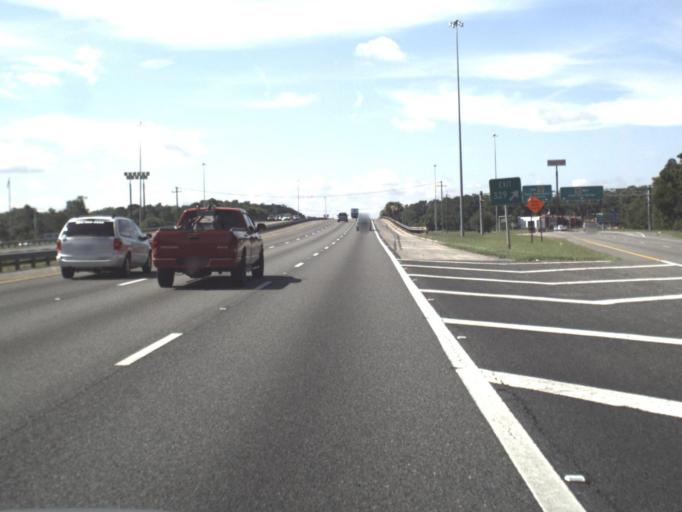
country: US
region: Florida
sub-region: Saint Johns County
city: Fruit Cove
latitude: 30.0689
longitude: -81.4986
